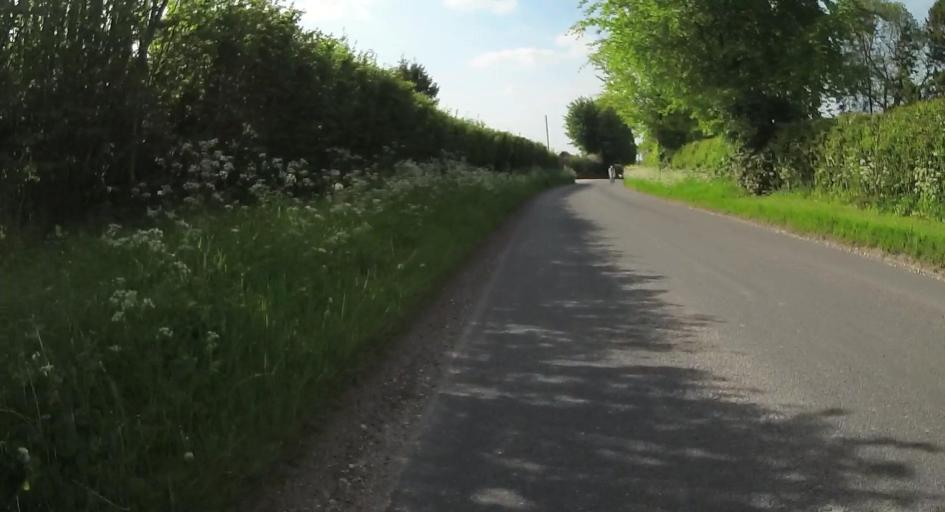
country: GB
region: England
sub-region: Hampshire
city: Four Marks
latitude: 51.1366
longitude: -1.0672
